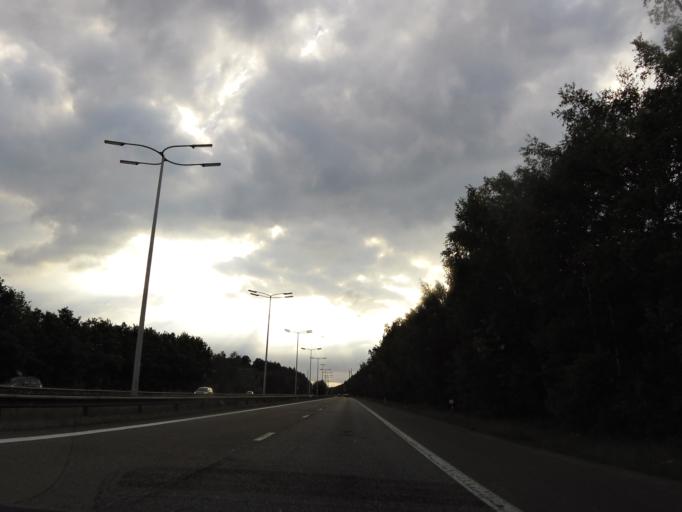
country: BE
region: Flanders
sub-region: Provincie Limburg
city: Maasmechelen
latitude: 50.9579
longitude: 5.6548
